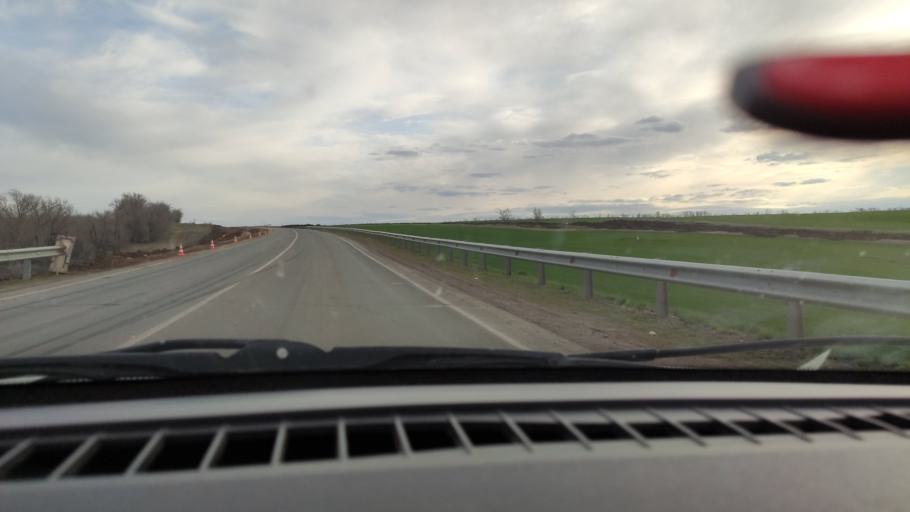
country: RU
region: Orenburg
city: Sakmara
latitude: 52.1861
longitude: 55.2946
